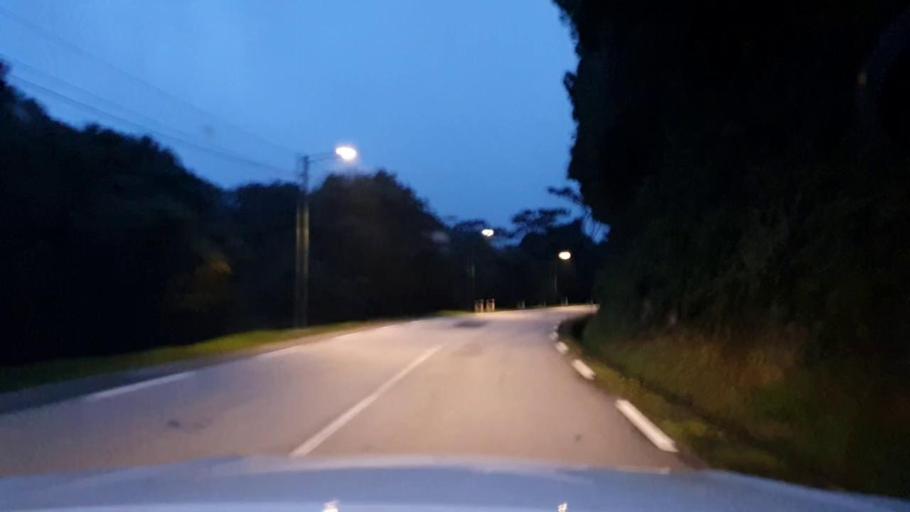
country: RW
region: Southern Province
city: Nzega
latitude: -2.5300
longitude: 29.3865
